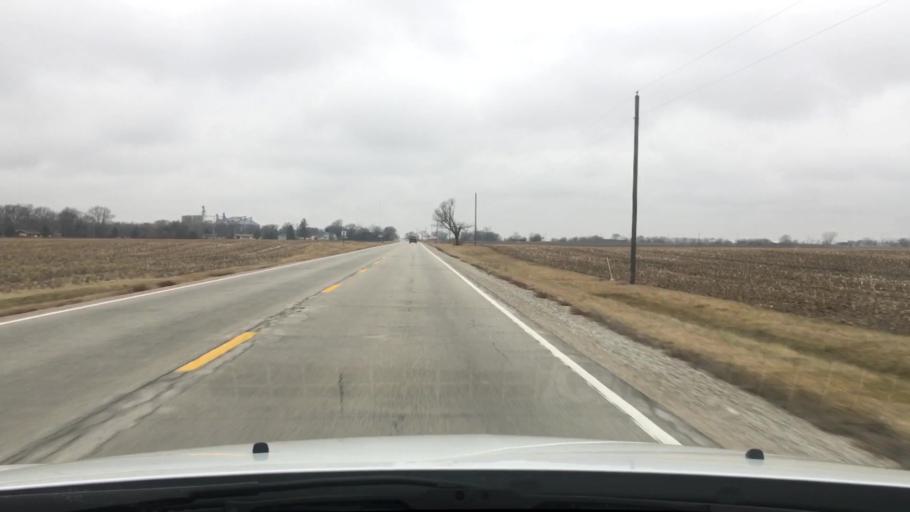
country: US
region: Illinois
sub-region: Iroquois County
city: Clifton
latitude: 40.8852
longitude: -87.9377
